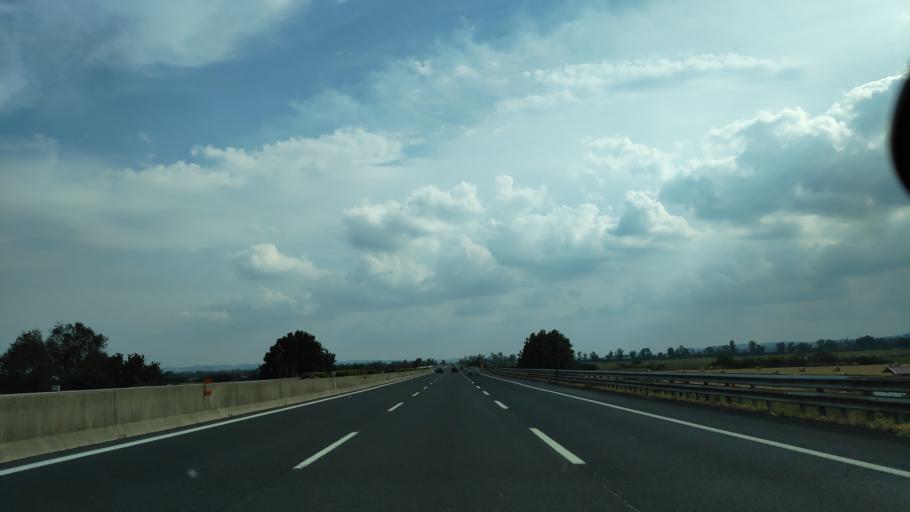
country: IT
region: Latium
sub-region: Citta metropolitana di Roma Capitale
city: Fiano Romano
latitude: 42.1442
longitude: 12.6223
